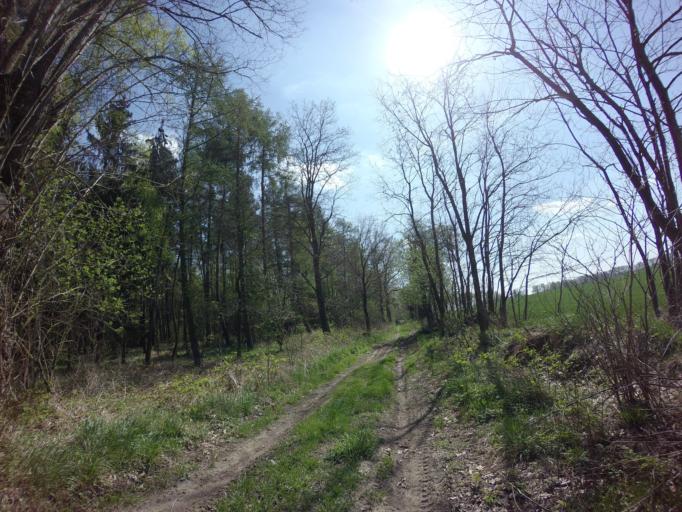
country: PL
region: West Pomeranian Voivodeship
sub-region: Powiat stargardzki
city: Suchan
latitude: 53.2051
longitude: 15.3055
